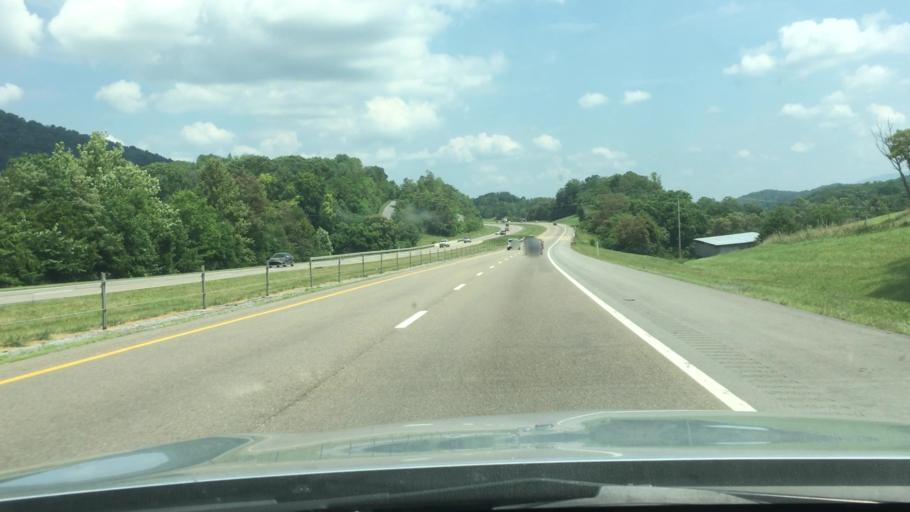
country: US
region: Tennessee
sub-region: Carter County
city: Pine Crest
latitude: 36.2502
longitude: -82.3247
